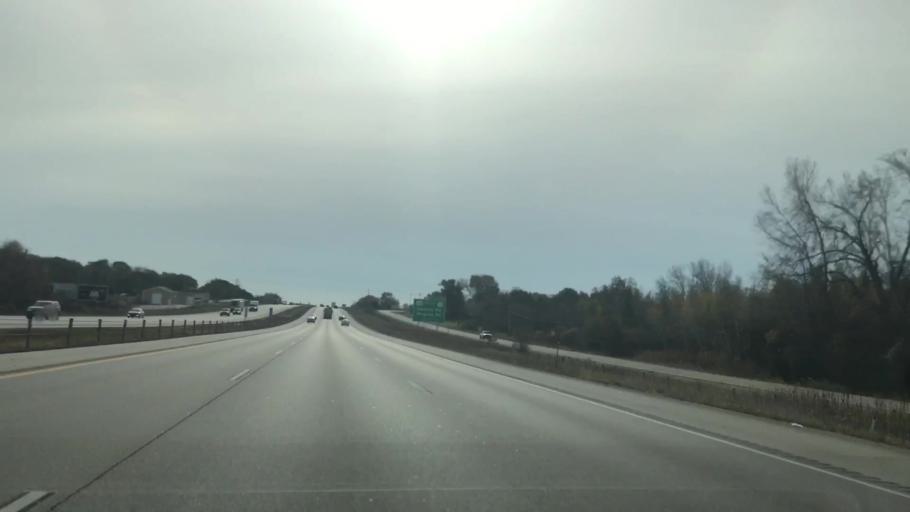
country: US
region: Wisconsin
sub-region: Washington County
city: Richfield
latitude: 43.2297
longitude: -88.1669
